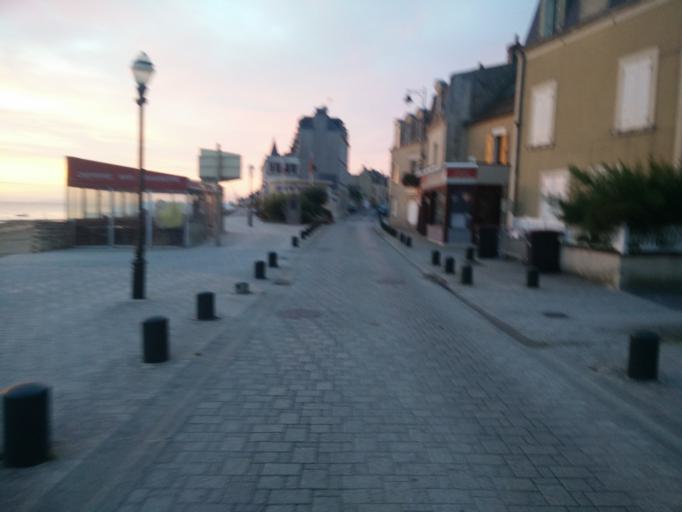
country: FR
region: Lower Normandy
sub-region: Departement du Calvados
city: Saint-Aubin-sur-Mer
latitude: 49.3320
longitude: -0.3936
